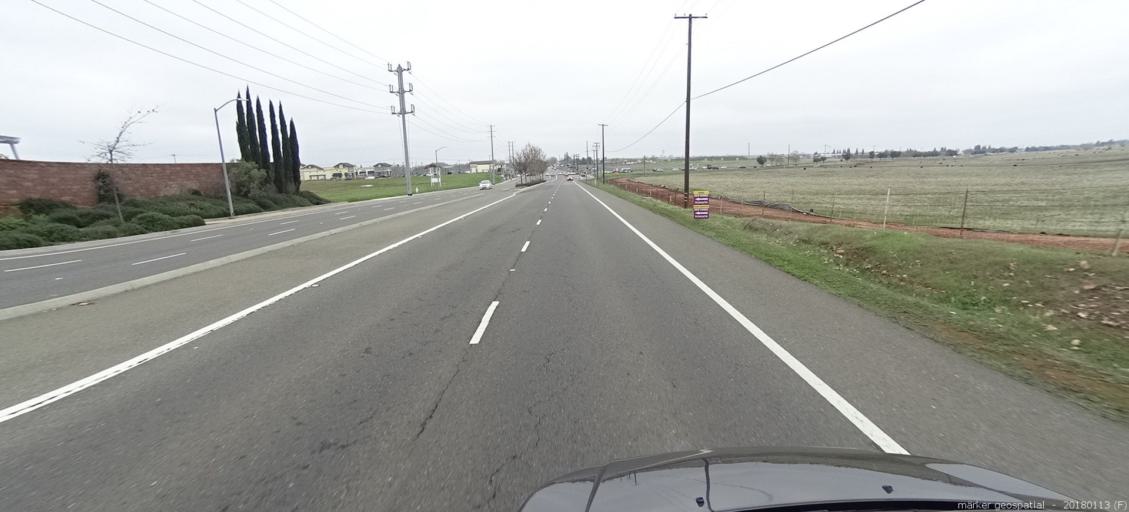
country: US
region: California
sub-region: Sacramento County
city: Gold River
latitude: 38.5595
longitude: -121.2395
